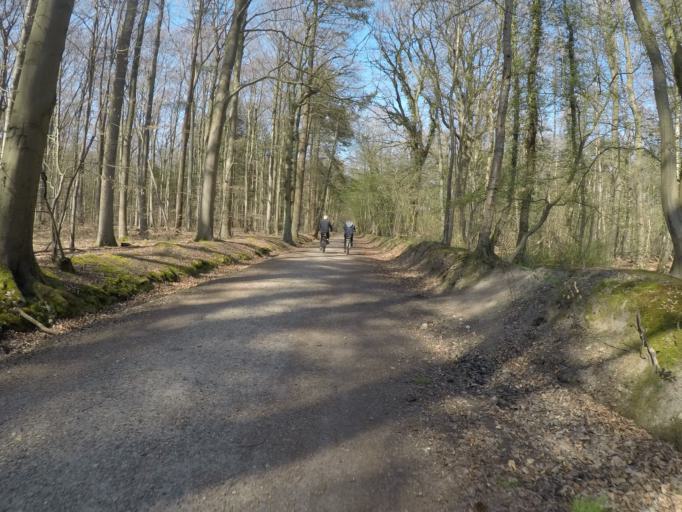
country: DE
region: Schleswig-Holstein
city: Rellingen
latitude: 53.6123
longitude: 9.7830
